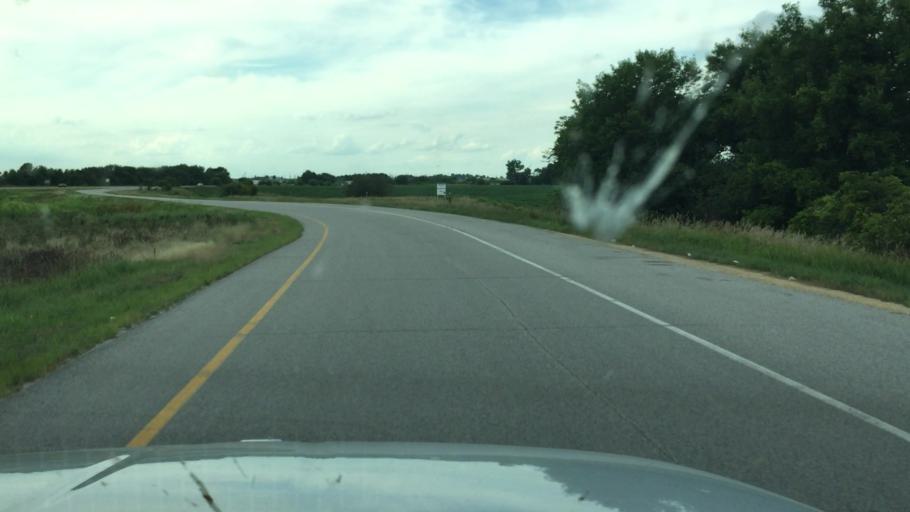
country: US
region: Iowa
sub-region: Scott County
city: Buffalo
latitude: 41.5386
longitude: -90.6746
